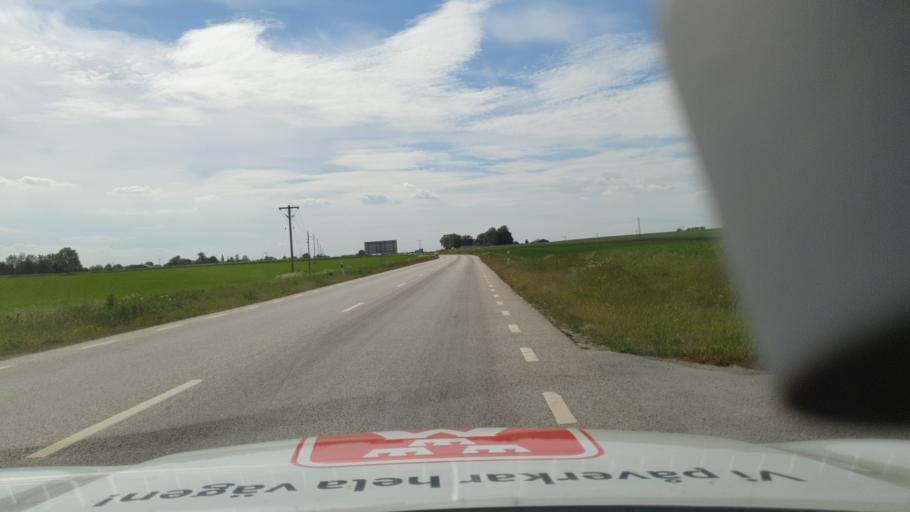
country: SE
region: Skane
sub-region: Simrishamns Kommun
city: Simrishamn
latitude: 55.5353
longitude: 14.2711
